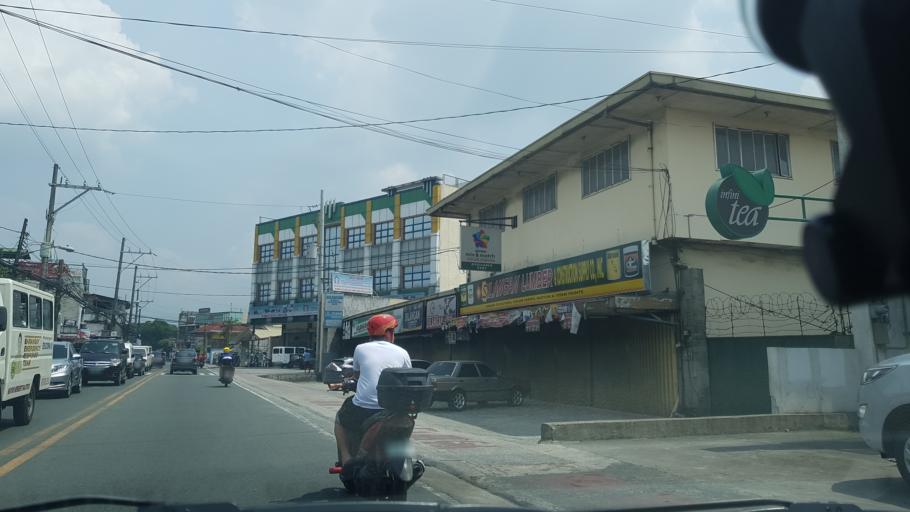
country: PH
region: Metro Manila
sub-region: Marikina
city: Calumpang
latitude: 14.6429
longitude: 121.0950
